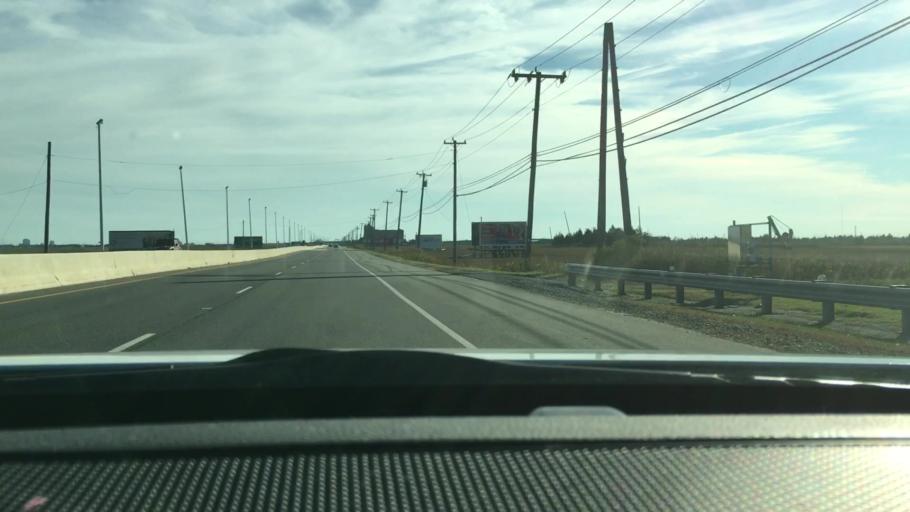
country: US
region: New Jersey
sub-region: Atlantic County
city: Absecon
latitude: 39.4146
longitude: -74.4914
